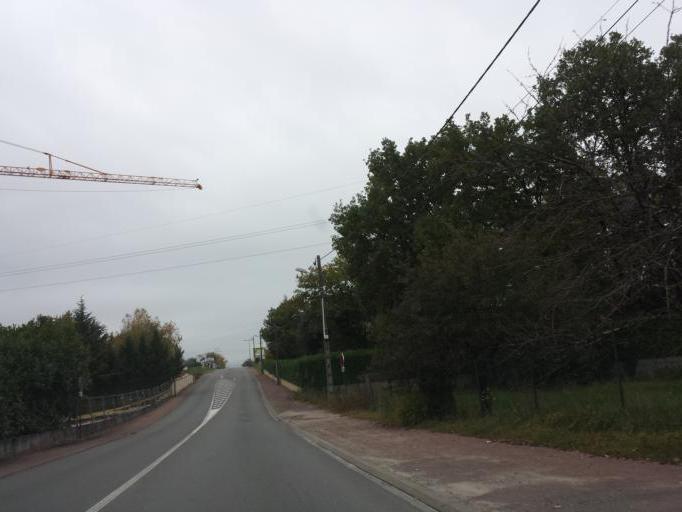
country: FR
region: Poitou-Charentes
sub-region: Departement de la Charente
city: Puymoyen
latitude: 45.6223
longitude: 0.1641
